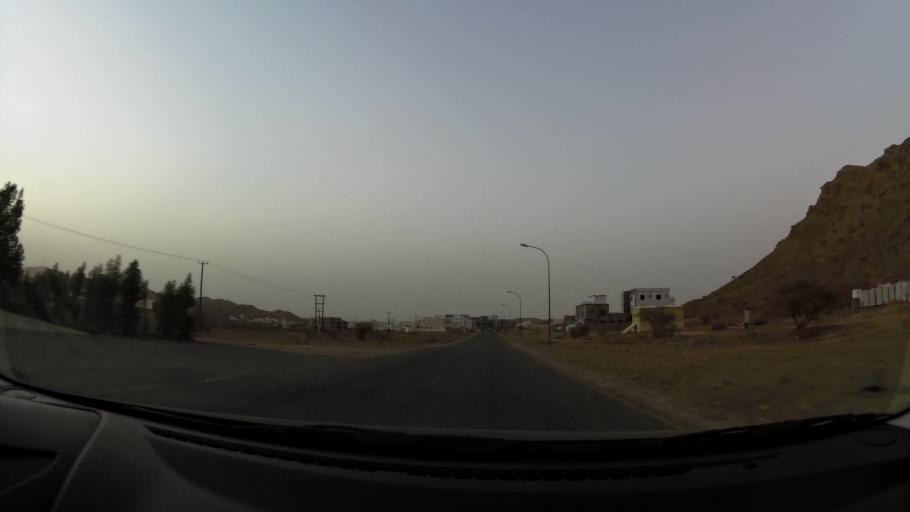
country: OM
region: Muhafazat Masqat
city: Bawshar
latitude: 23.5005
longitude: 58.3445
